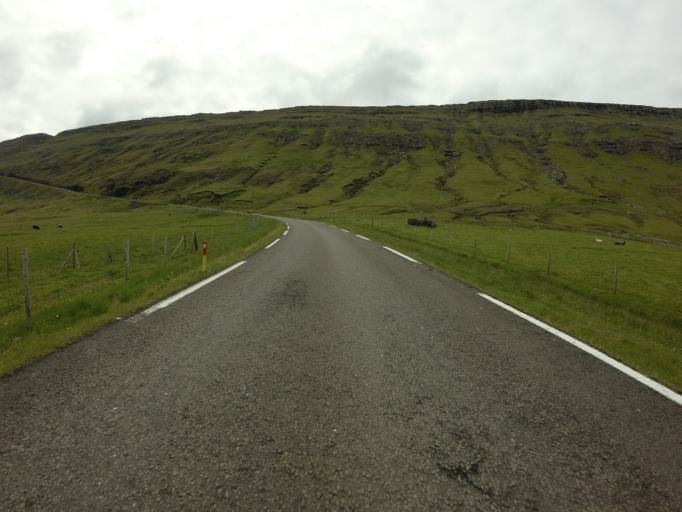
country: FO
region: Suduroy
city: Tvoroyri
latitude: 61.6262
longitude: -6.9433
